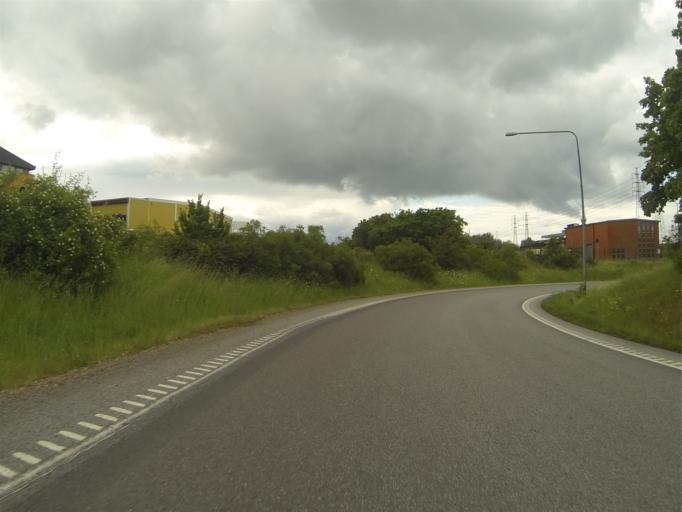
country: SE
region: Skane
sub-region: Burlovs Kommun
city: Arloev
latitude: 55.6227
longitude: 13.0562
